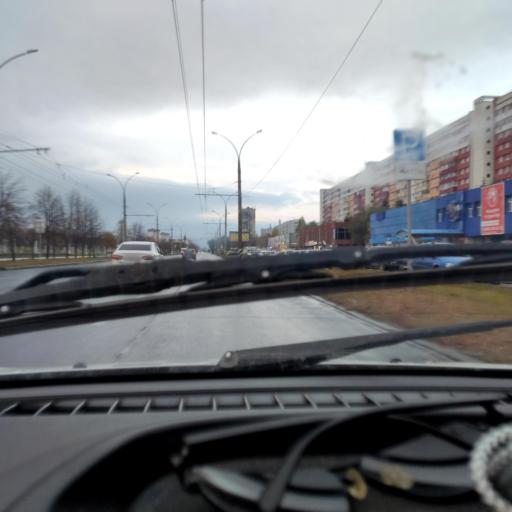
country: RU
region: Samara
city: Tol'yatti
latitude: 53.5137
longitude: 49.2721
